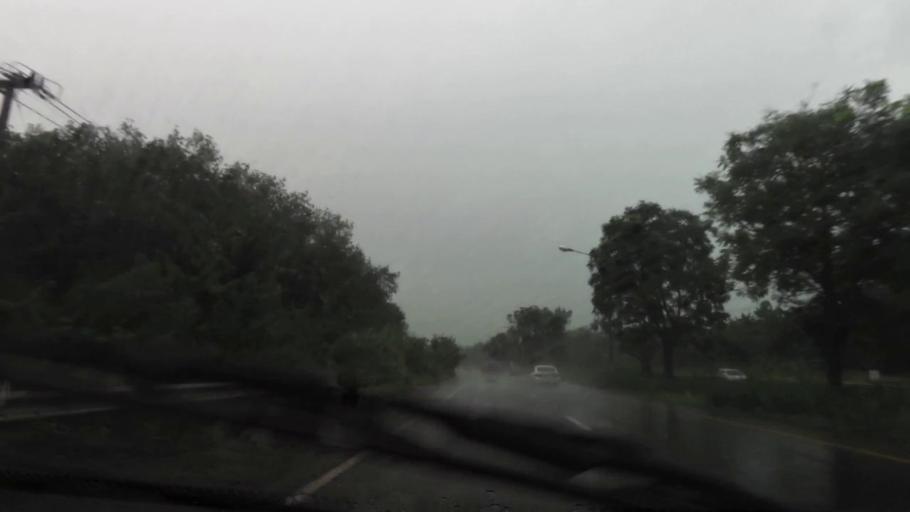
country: TH
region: Rayong
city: Wang Chan
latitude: 13.0068
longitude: 101.4806
